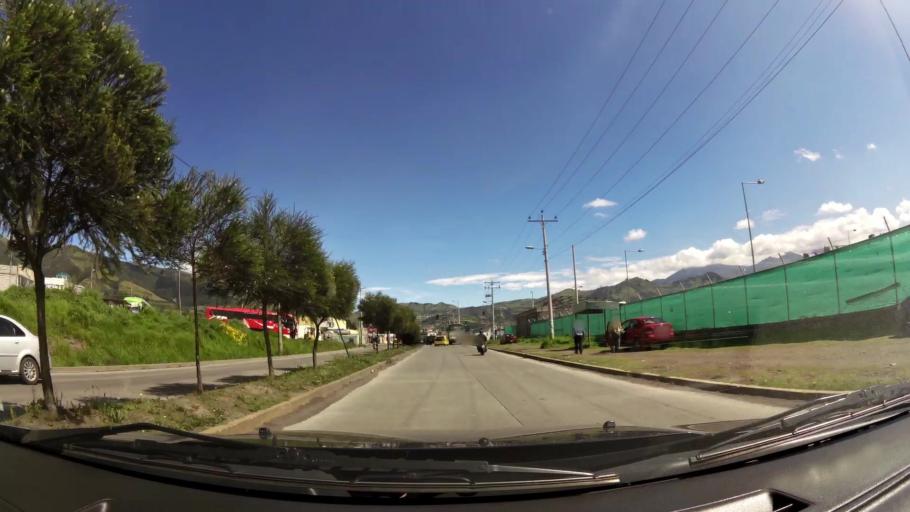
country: EC
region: Pichincha
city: Quito
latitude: -0.3014
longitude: -78.5558
